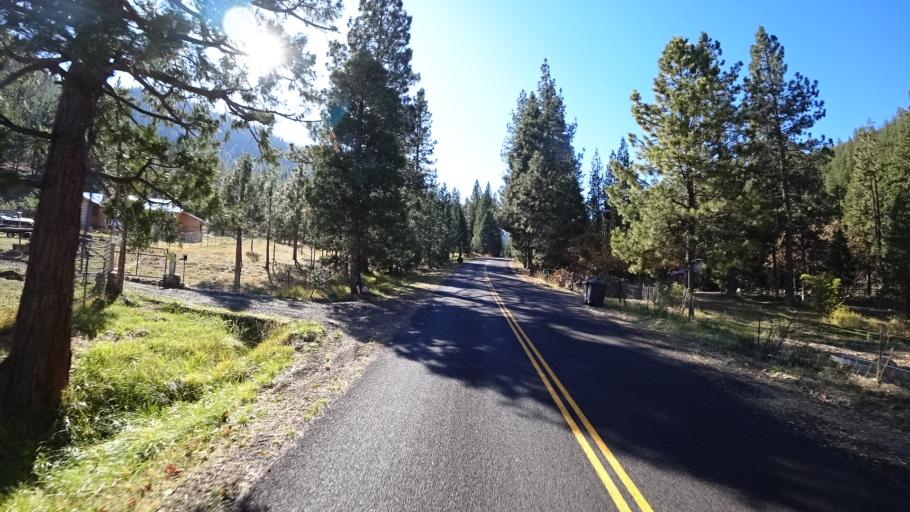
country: US
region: California
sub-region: Siskiyou County
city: Weed
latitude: 41.4243
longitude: -122.4999
